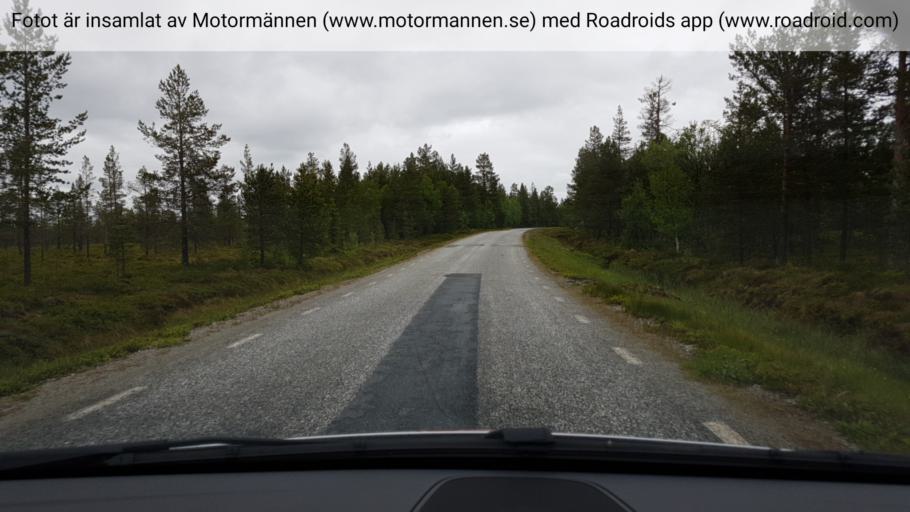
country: SE
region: Jaemtland
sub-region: Harjedalens Kommun
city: Sveg
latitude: 62.3342
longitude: 13.4265
